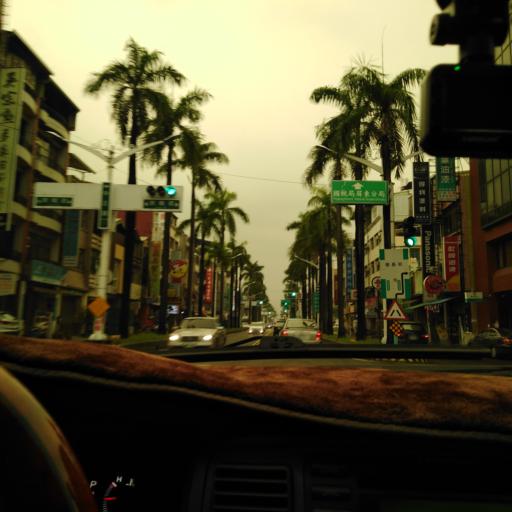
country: TW
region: Taiwan
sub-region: Pingtung
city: Pingtung
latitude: 22.6771
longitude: 120.4903
